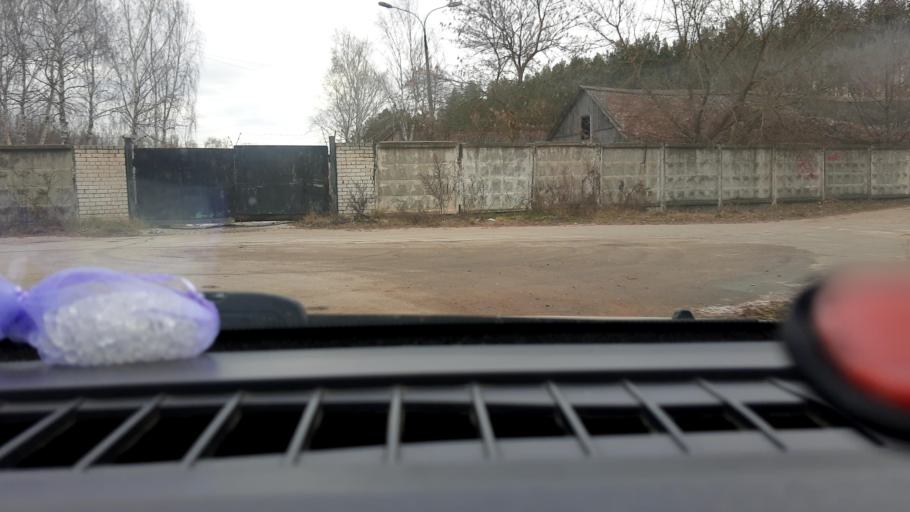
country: RU
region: Nizjnij Novgorod
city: Gorbatovka
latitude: 56.3815
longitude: 43.7778
